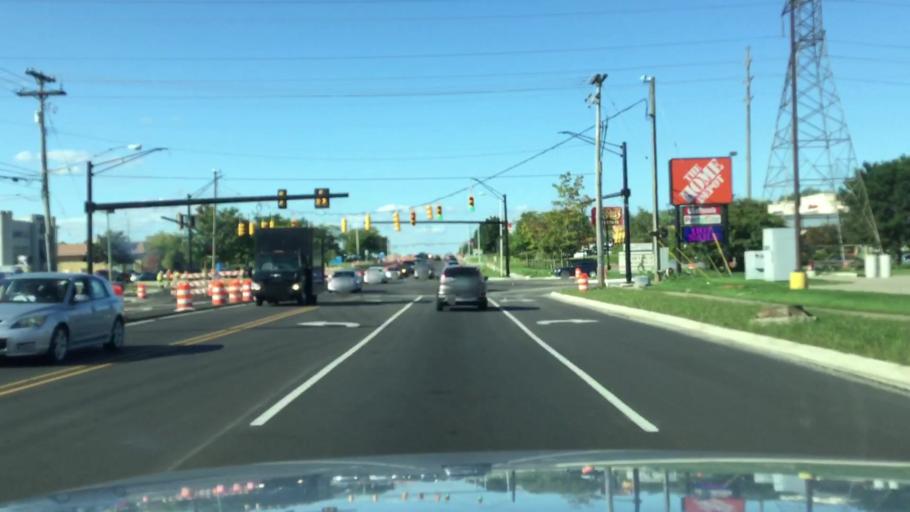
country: US
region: Michigan
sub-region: Kalamazoo County
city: Portage
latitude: 42.2188
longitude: -85.5894
